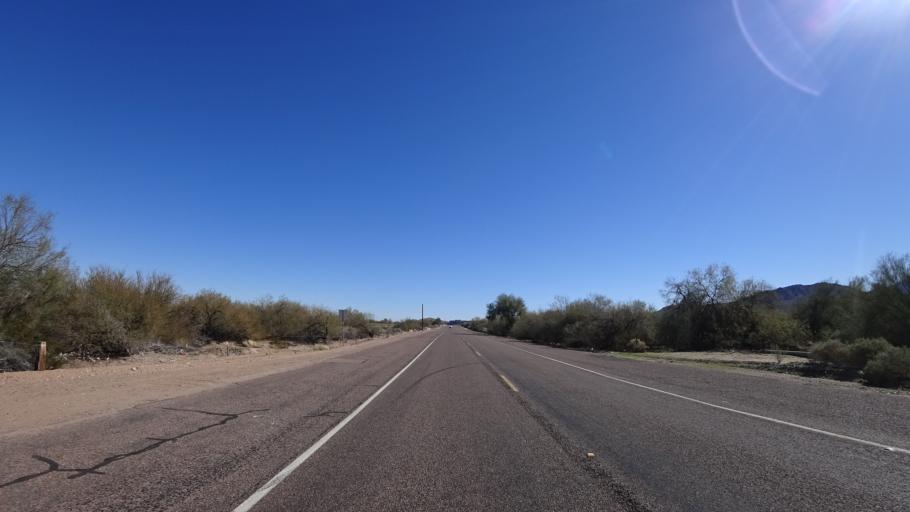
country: US
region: Arizona
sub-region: Maricopa County
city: Avondale
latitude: 33.3756
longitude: -112.3419
